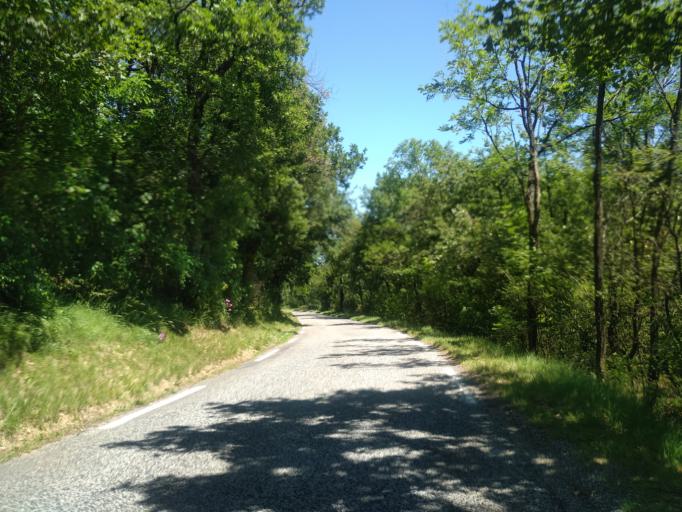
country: FR
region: Rhone-Alpes
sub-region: Departement du Rhone
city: Albigny-sur-Saone
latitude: 45.8507
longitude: 4.8158
